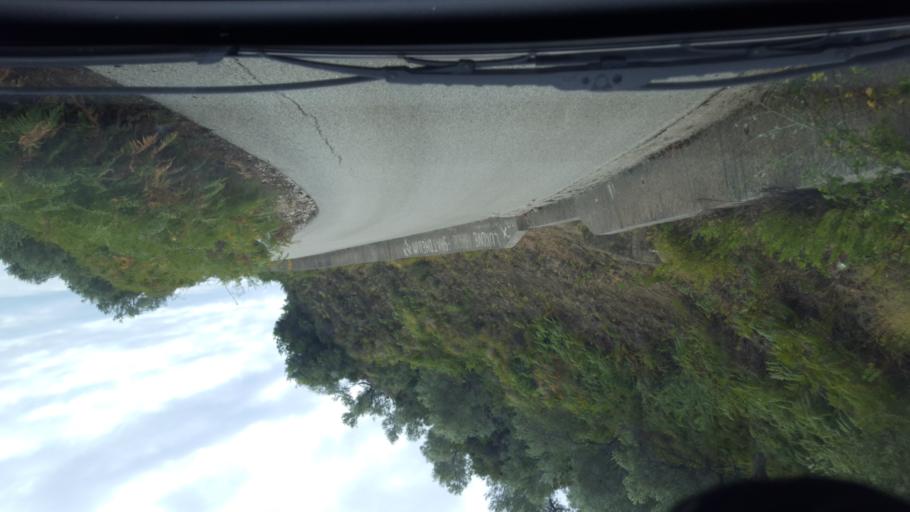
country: AL
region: Vlore
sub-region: Rrethi i Sarandes
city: Lukove
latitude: 39.9839
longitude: 19.9157
